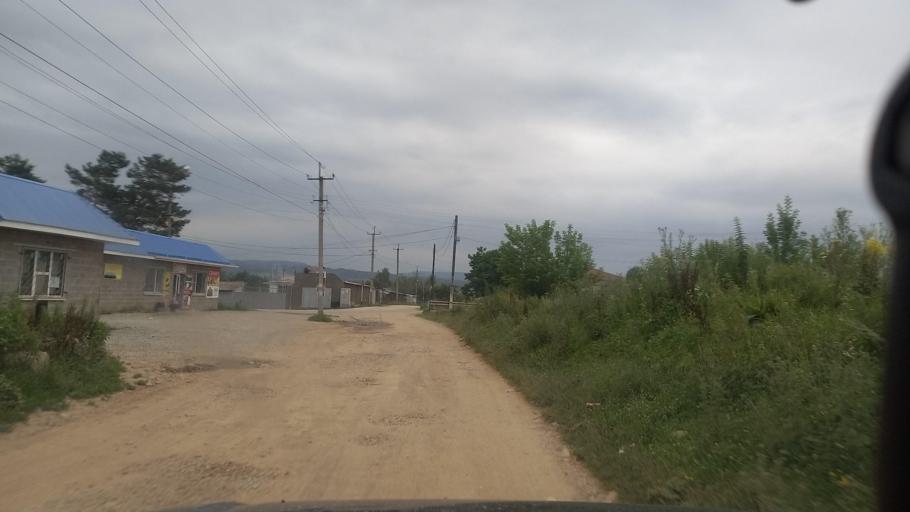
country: RU
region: Karachayevo-Cherkesiya
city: Pregradnaya
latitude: 43.9481
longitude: 41.1862
